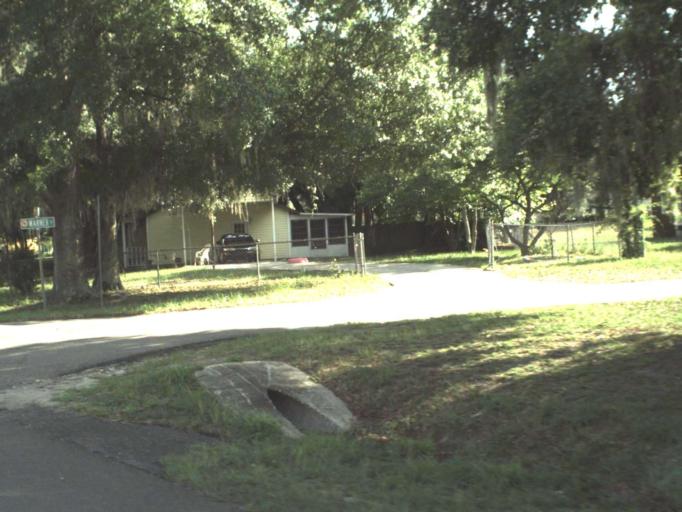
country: US
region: Florida
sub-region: Lake County
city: Groveland
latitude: 28.5518
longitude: -81.8516
